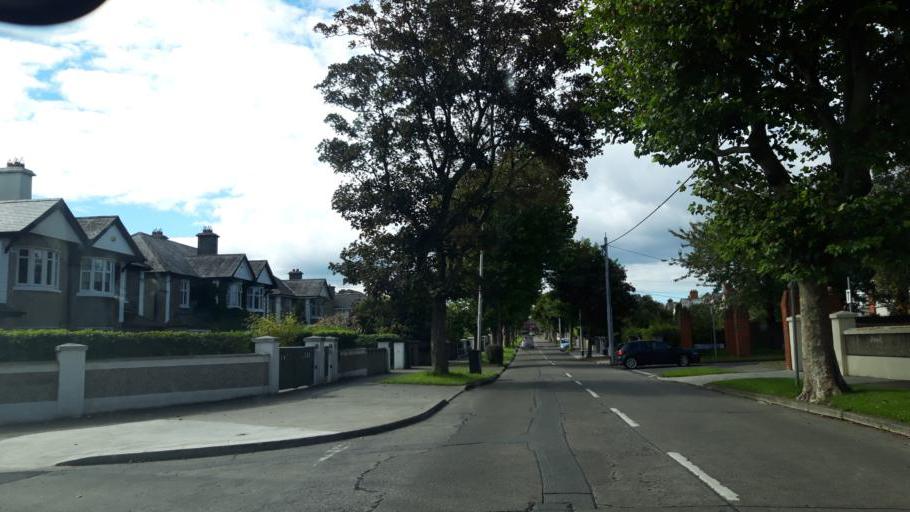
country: IE
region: Leinster
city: Dollymount
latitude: 53.3667
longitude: -6.1903
